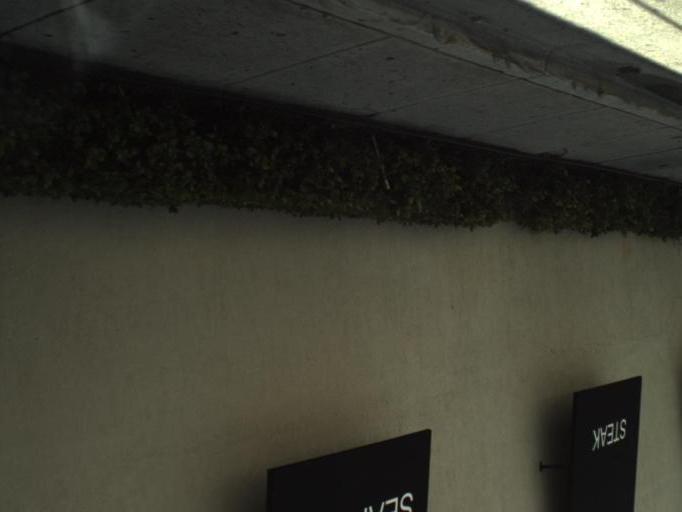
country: US
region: Florida
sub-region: Broward County
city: Hollywood
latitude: 26.0163
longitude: -80.1174
